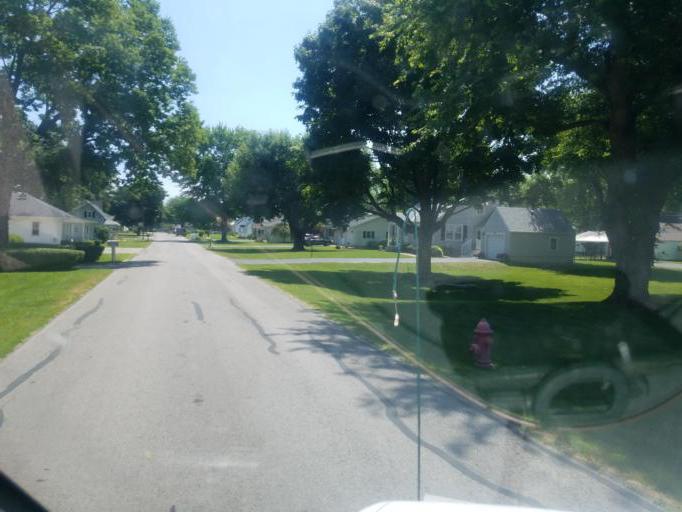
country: US
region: Ohio
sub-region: Logan County
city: West Liberty
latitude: 40.2563
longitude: -83.7544
